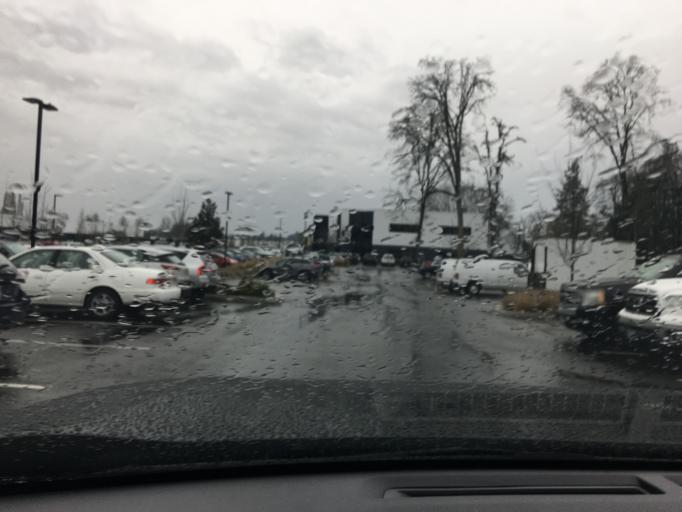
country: US
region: Oregon
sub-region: Washington County
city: Aloha
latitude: 45.4994
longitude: -122.8366
